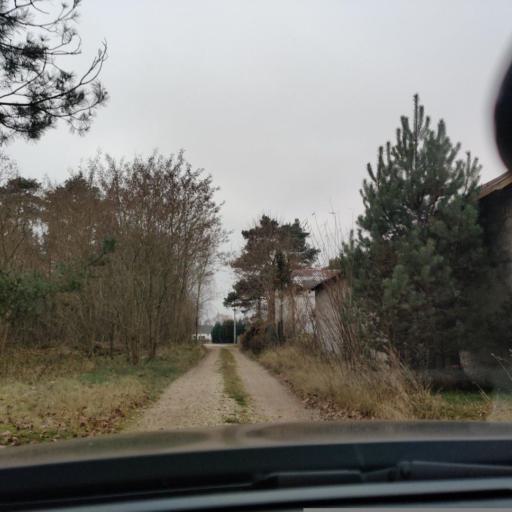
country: PL
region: Lodz Voivodeship
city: Zabia Wola
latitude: 52.0251
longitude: 20.6405
